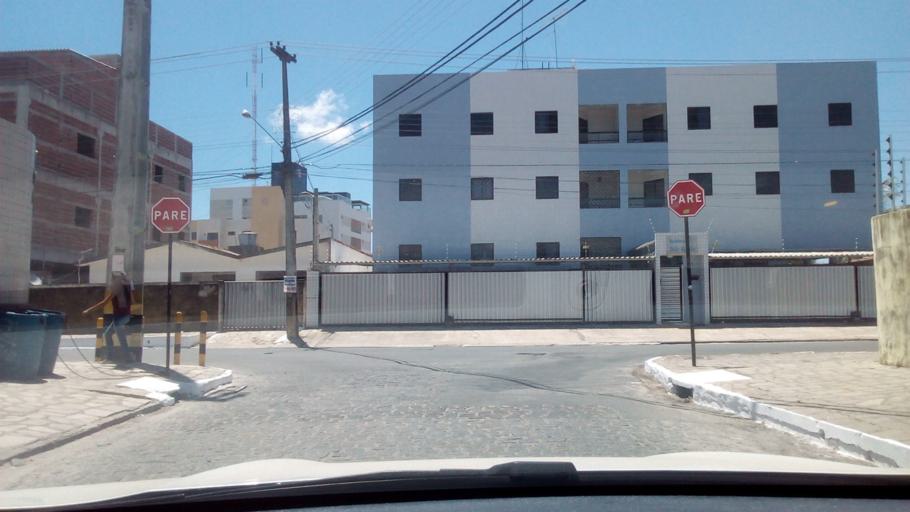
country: BR
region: Paraiba
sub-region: Joao Pessoa
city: Joao Pessoa
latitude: -7.1594
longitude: -34.8372
